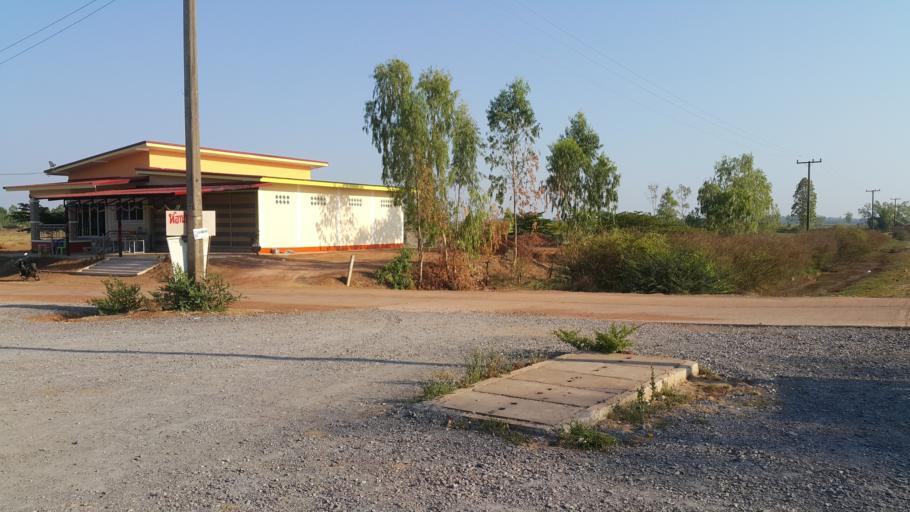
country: TH
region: Changwat Udon Thani
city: Ban Na Muang
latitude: 17.2168
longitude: 103.0667
